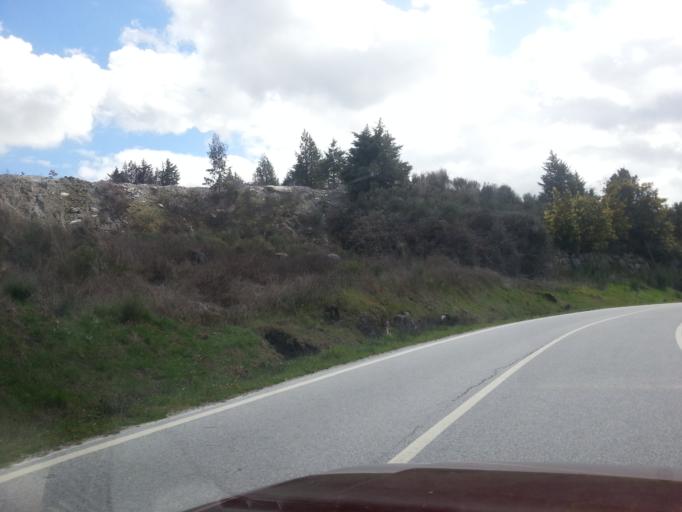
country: PT
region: Guarda
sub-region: Fornos de Algodres
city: Fornos de Algodres
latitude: 40.5989
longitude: -7.5302
